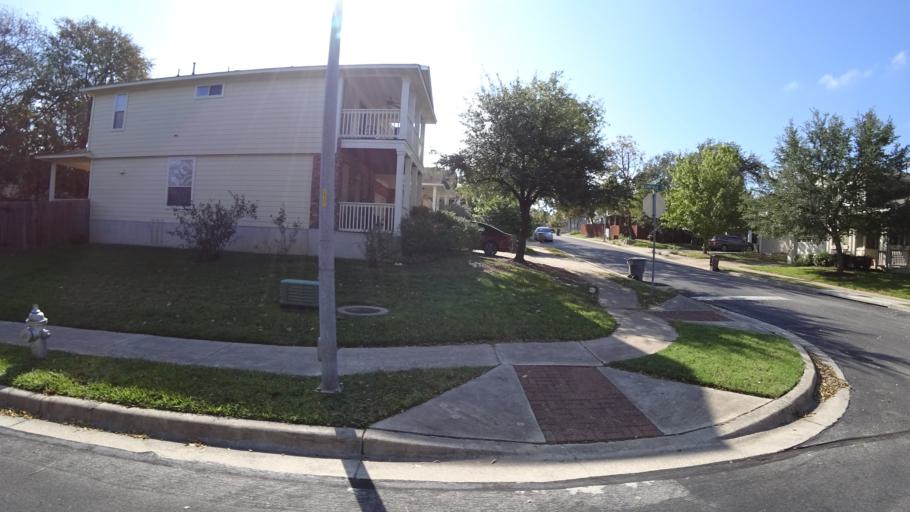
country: US
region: Texas
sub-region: Travis County
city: Shady Hollow
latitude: 30.1914
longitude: -97.8188
